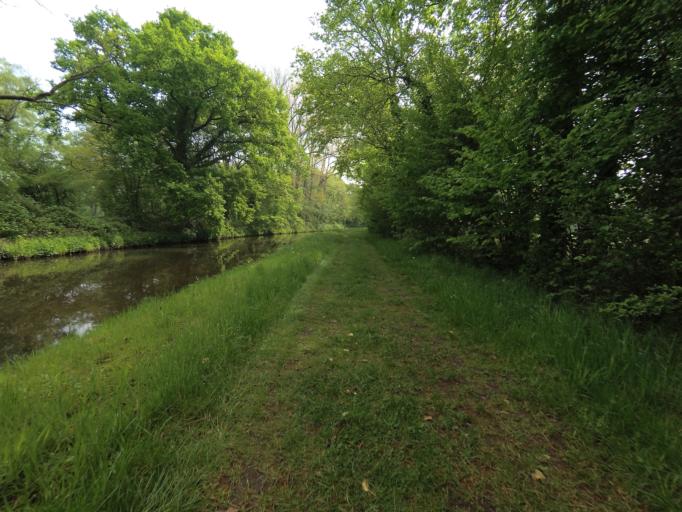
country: NL
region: Gelderland
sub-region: Gemeente Barneveld
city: Terschuur
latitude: 52.1439
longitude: 5.5282
